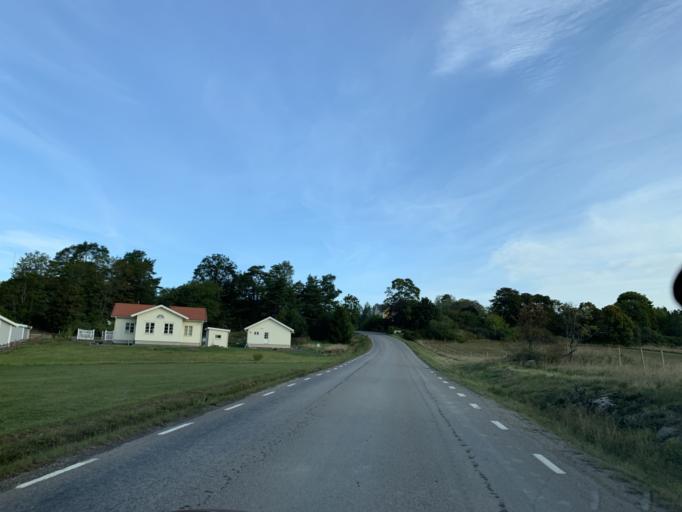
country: SE
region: Stockholm
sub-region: Haninge Kommun
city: Jordbro
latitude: 59.0639
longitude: 18.0666
